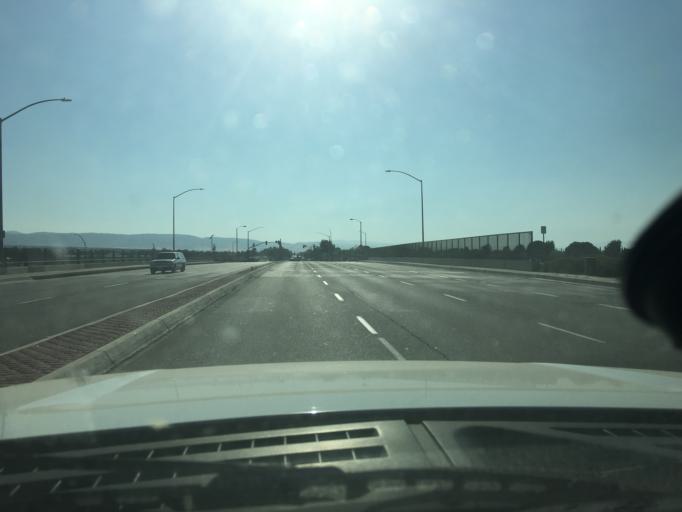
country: US
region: California
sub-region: Los Angeles County
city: Lancaster
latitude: 34.6604
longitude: -118.1524
